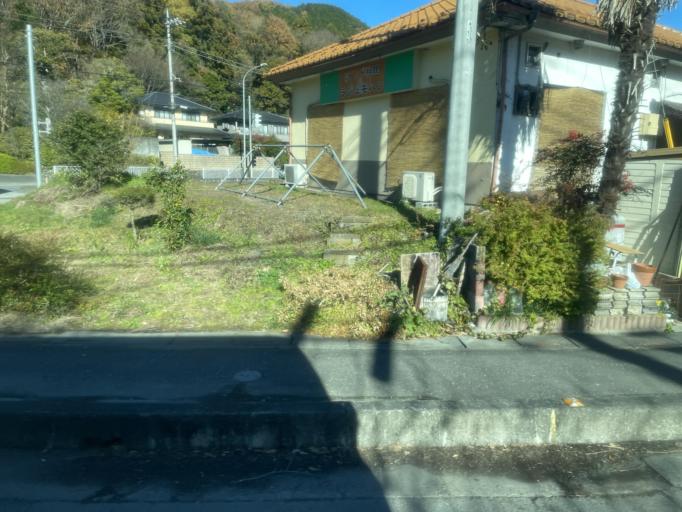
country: JP
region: Saitama
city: Ogawa
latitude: 36.0439
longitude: 139.2345
